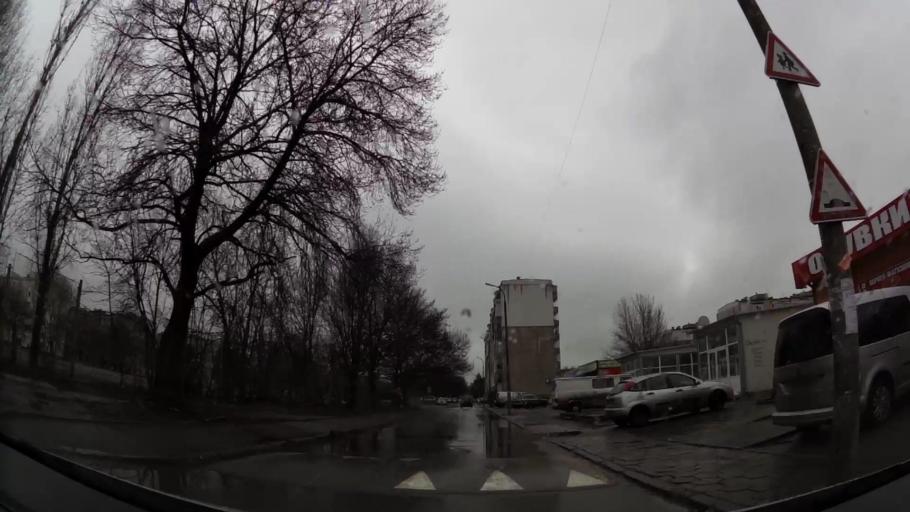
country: BG
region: Sofia-Capital
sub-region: Stolichna Obshtina
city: Sofia
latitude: 42.6669
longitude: 23.3967
